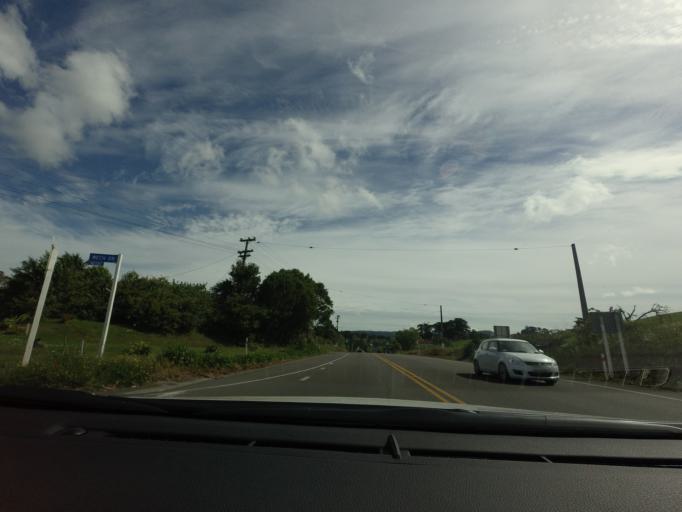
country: NZ
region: Auckland
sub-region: Auckland
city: Warkworth
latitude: -36.4125
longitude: 174.6575
